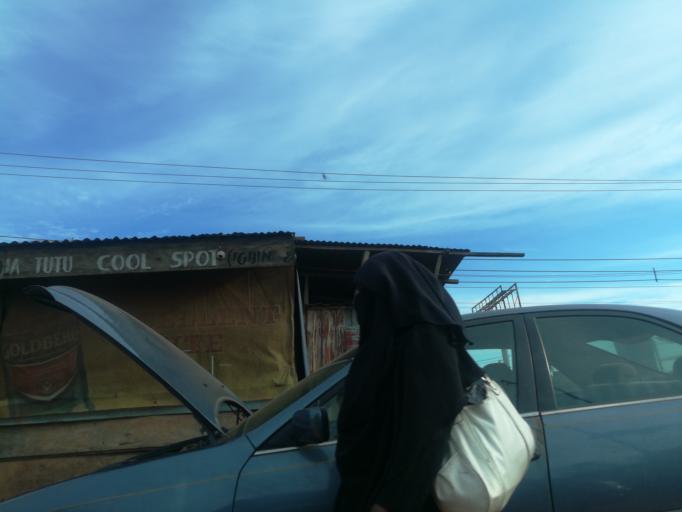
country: NG
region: Oyo
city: Ibadan
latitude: 7.3403
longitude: 3.9053
